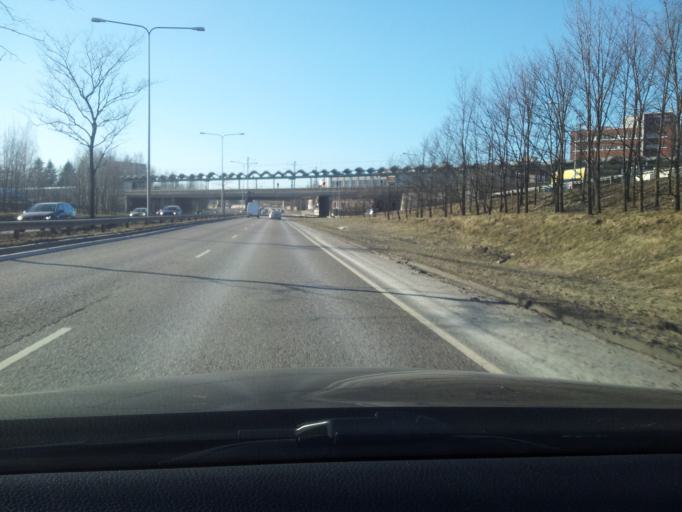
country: FI
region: Uusimaa
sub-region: Helsinki
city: Vantaa
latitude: 60.2418
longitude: 24.9959
